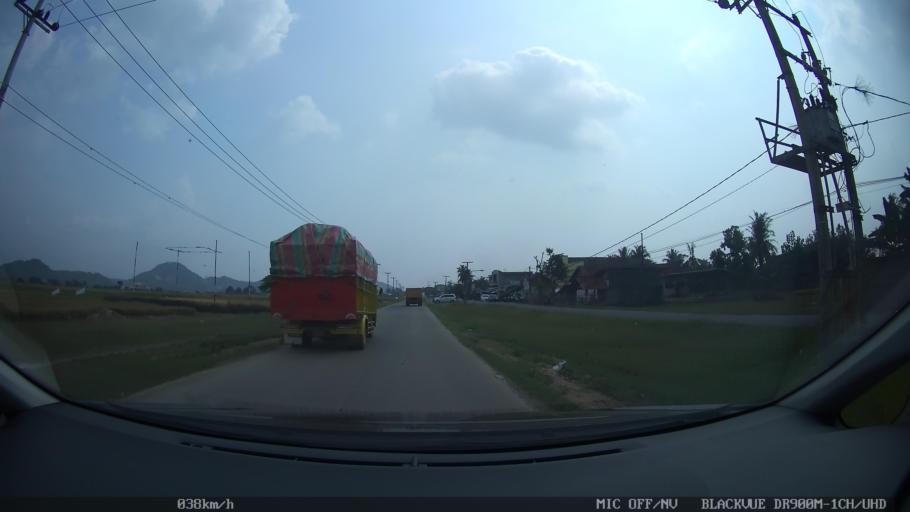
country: ID
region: Lampung
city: Pringsewu
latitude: -5.3600
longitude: 105.0077
